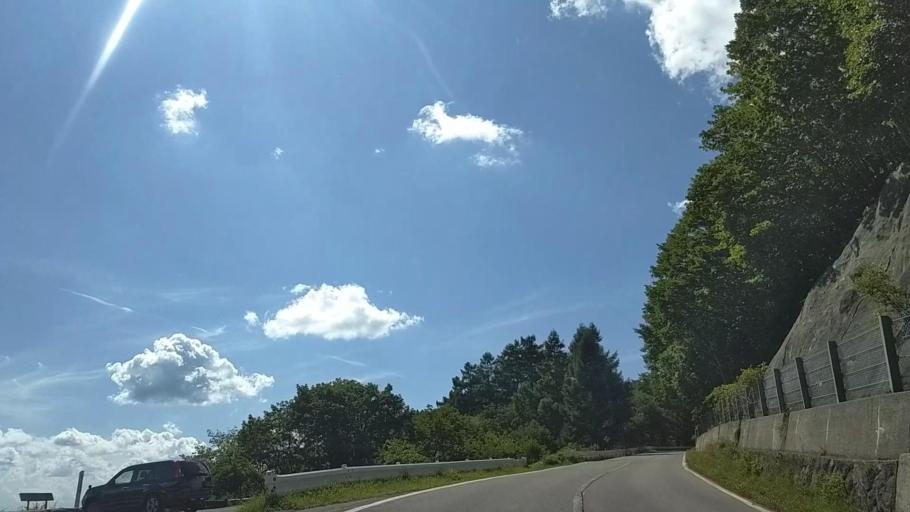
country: JP
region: Nagano
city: Chino
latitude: 36.0816
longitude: 138.2869
